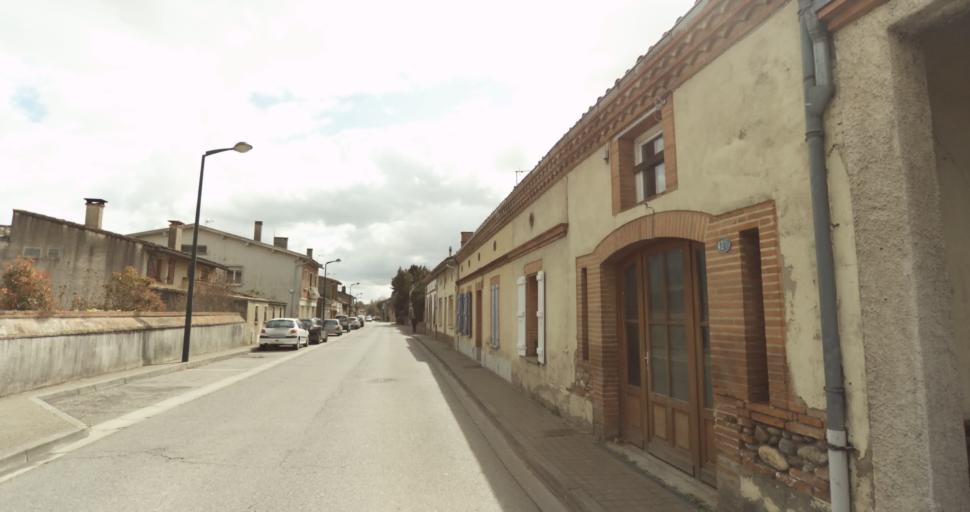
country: FR
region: Midi-Pyrenees
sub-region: Departement de la Haute-Garonne
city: Auterive
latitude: 43.3533
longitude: 1.4714
